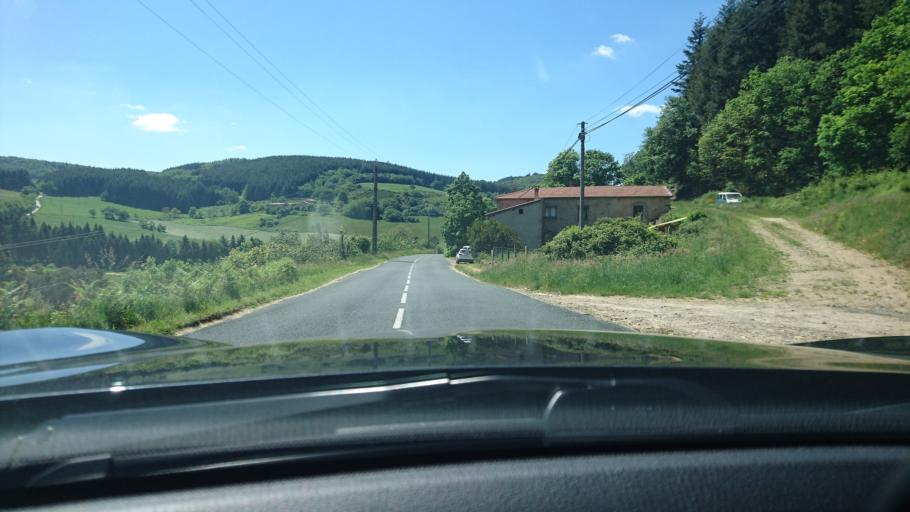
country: FR
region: Rhone-Alpes
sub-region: Departement du Rhone
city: Courzieu
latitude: 45.7097
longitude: 4.5864
